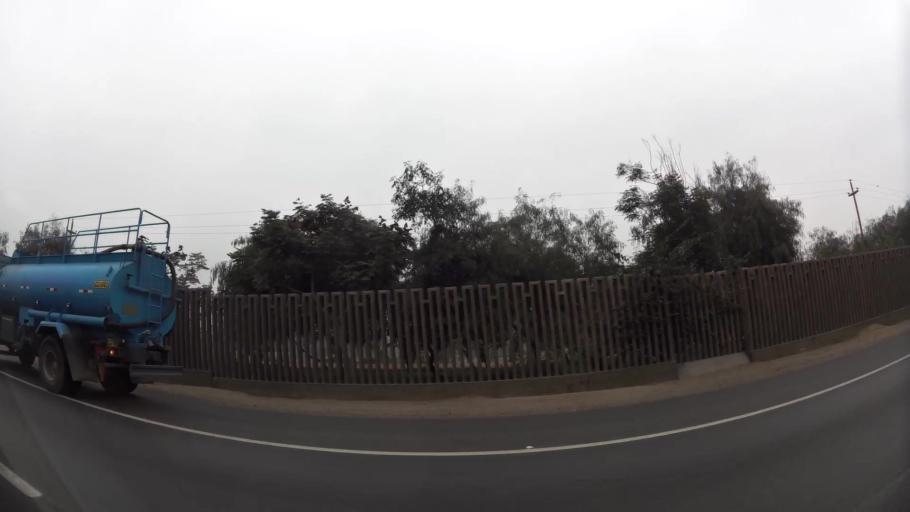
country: PE
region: Lima
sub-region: Lima
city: Vitarte
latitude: -12.0213
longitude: -76.9310
